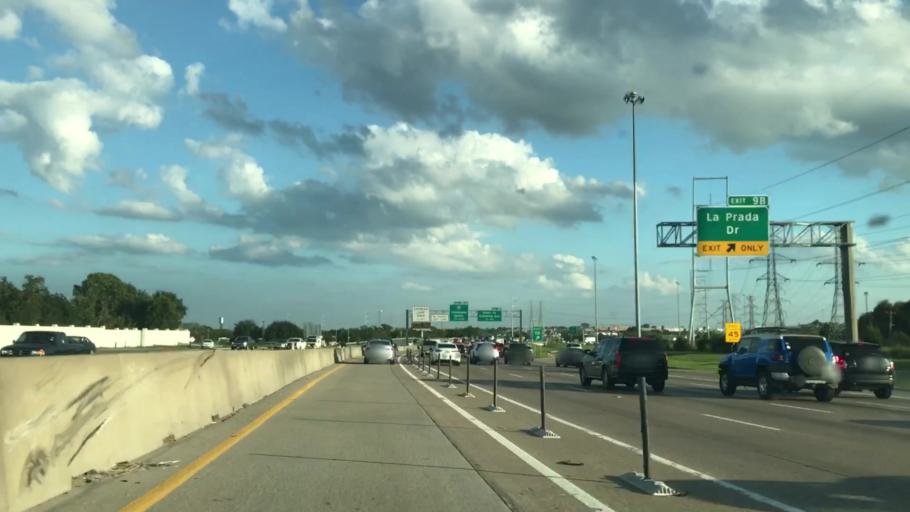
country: US
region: Texas
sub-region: Dallas County
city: Garland
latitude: 32.8465
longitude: -96.6371
